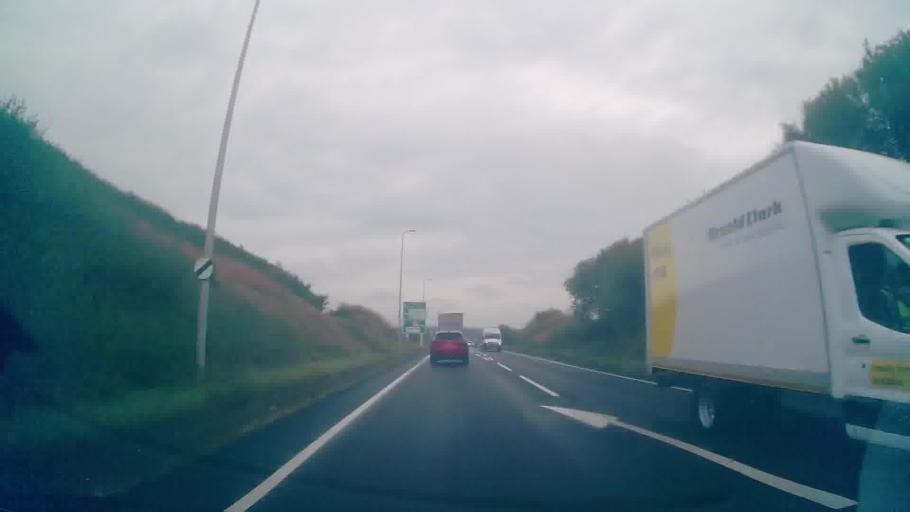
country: GB
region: Scotland
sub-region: Dumfries and Galloway
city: Lochmaben
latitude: 55.0337
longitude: -3.4126
